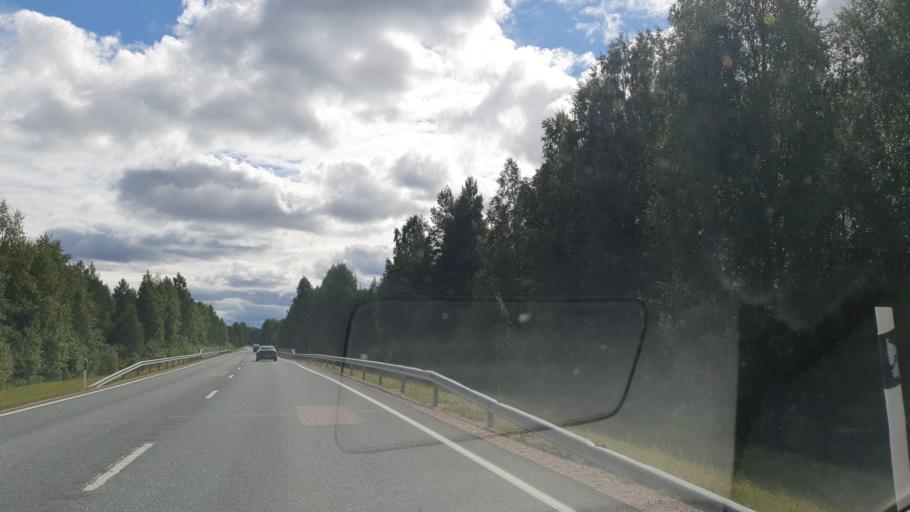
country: FI
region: Kainuu
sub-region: Kajaani
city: Kajaani
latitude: 64.1155
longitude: 27.4485
